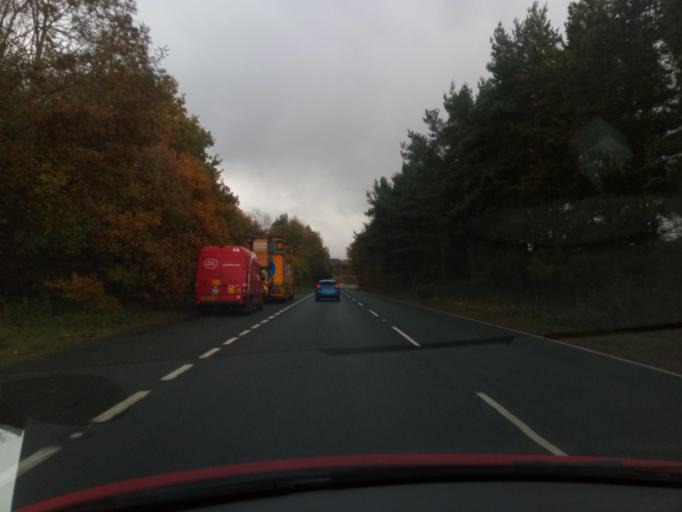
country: GB
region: England
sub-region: Northumberland
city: Stocksfield
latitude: 54.9594
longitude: -1.9554
